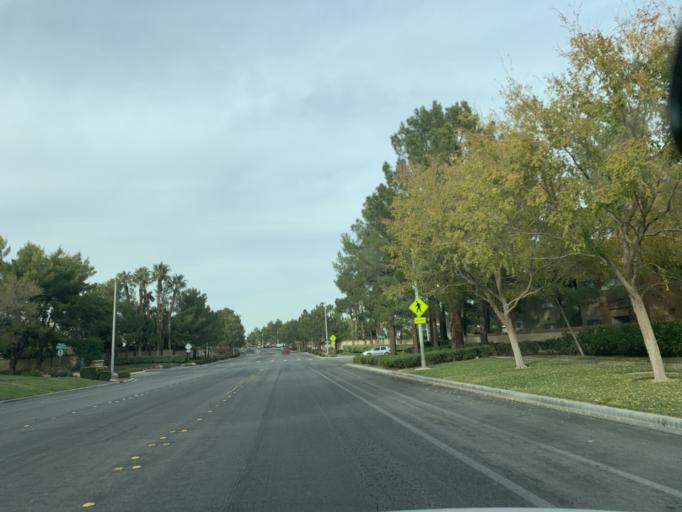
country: US
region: Nevada
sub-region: Clark County
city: Summerlin South
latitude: 36.1463
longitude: -115.3068
